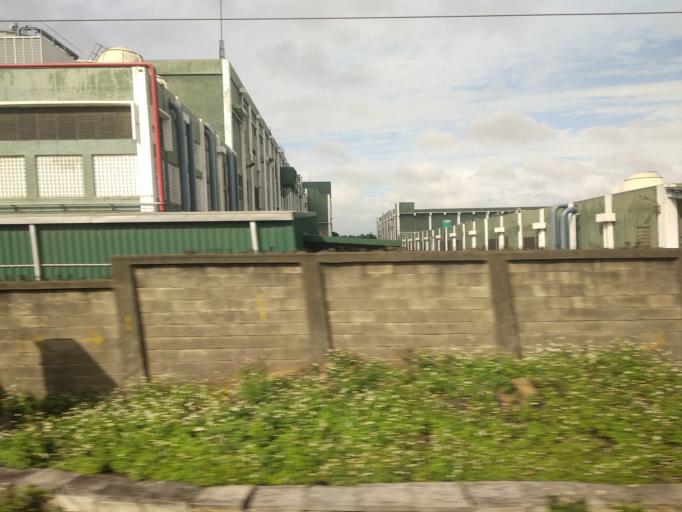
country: TW
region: Taiwan
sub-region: Hsinchu
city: Zhubei
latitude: 24.9130
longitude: 121.0497
